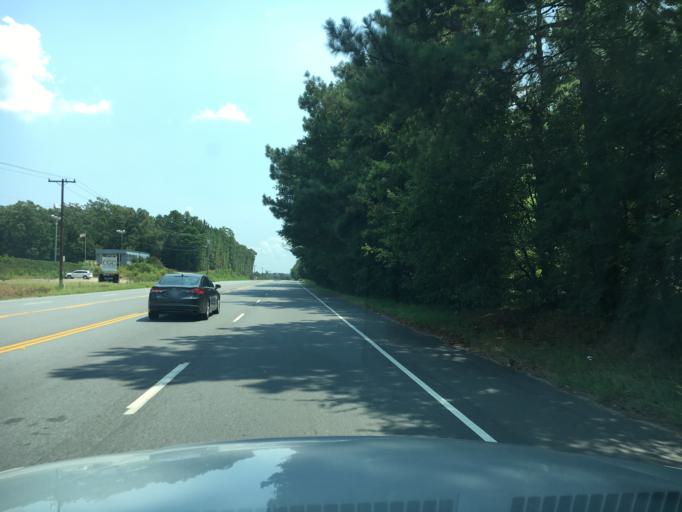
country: US
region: South Carolina
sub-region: Anderson County
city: Pendleton
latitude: 34.6167
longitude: -82.7730
